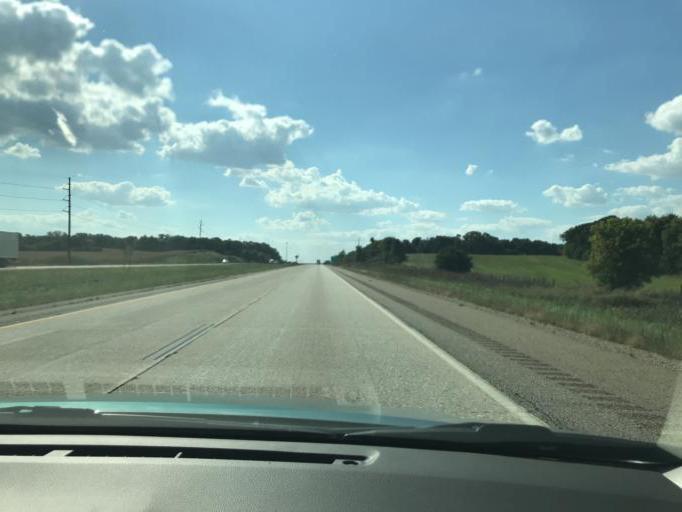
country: US
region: Wisconsin
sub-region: Walworth County
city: Darien
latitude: 42.6175
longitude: -88.6918
